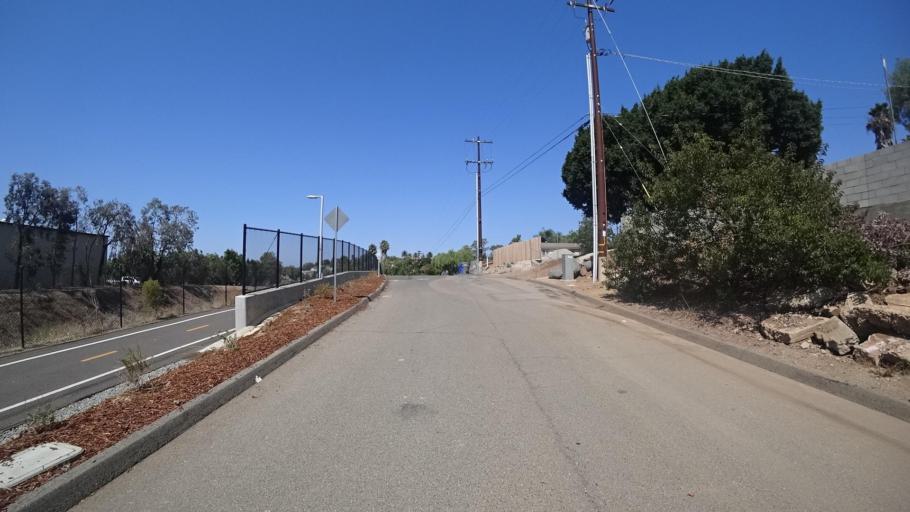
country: US
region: California
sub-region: San Diego County
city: Lake San Marcos
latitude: 33.1642
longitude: -117.1998
